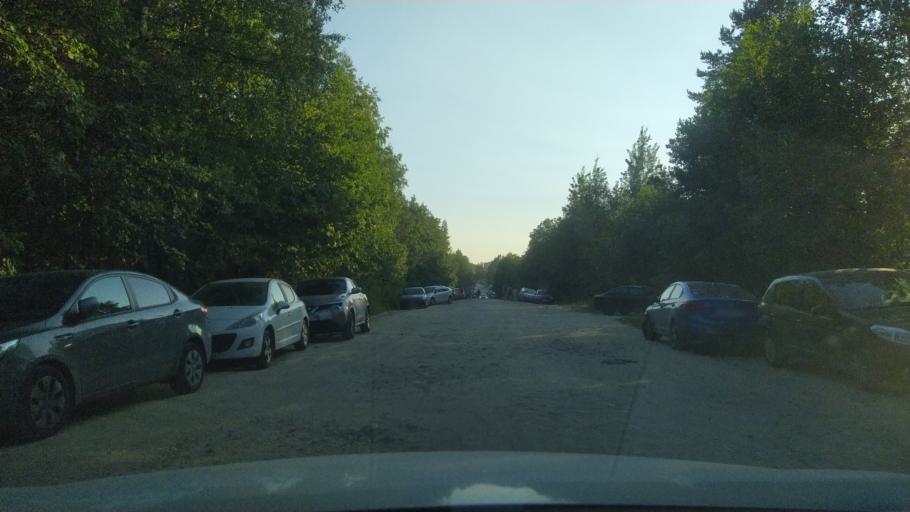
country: RU
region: Leningrad
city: Toksovo
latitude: 60.1133
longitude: 30.5138
